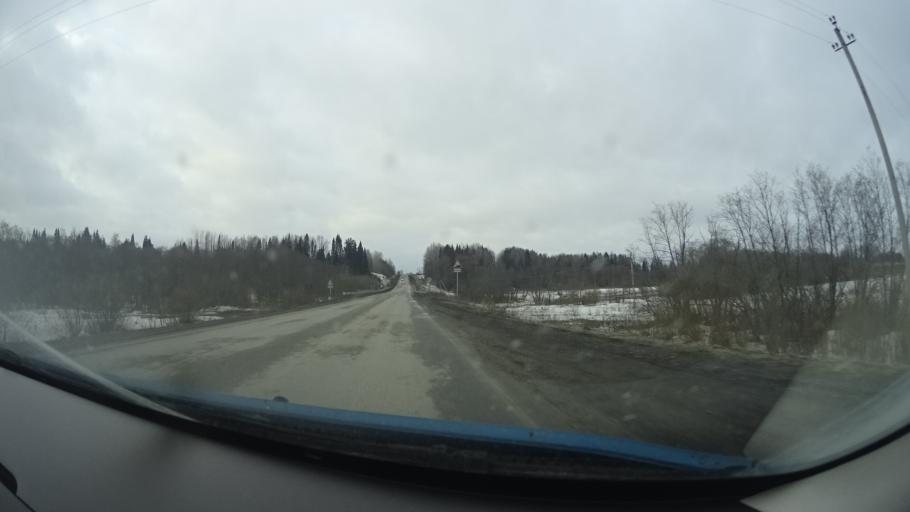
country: RU
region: Perm
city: Osa
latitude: 57.2994
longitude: 55.6143
